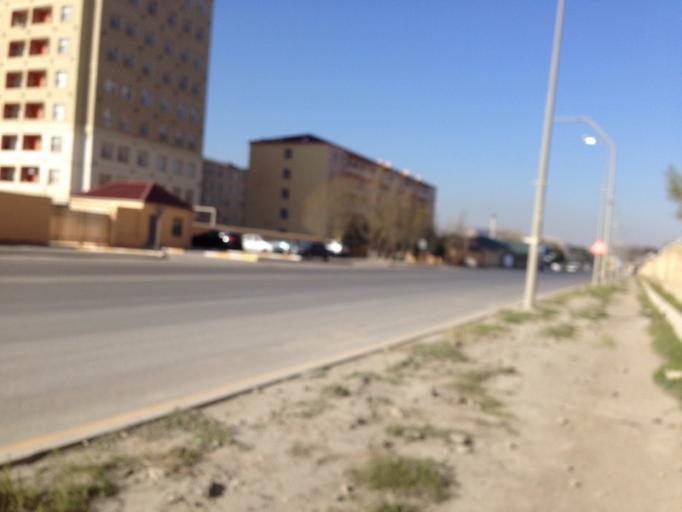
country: AZ
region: Baki
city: Baku
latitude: 40.4144
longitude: 49.8699
